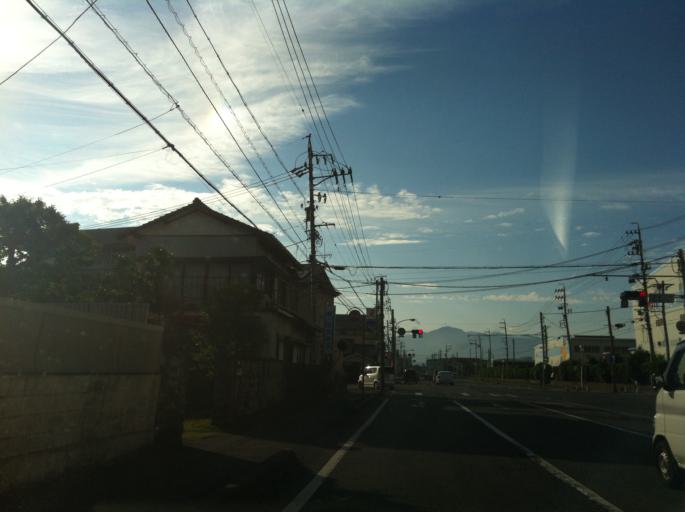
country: JP
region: Shizuoka
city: Shizuoka-shi
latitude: 34.9882
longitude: 138.4983
